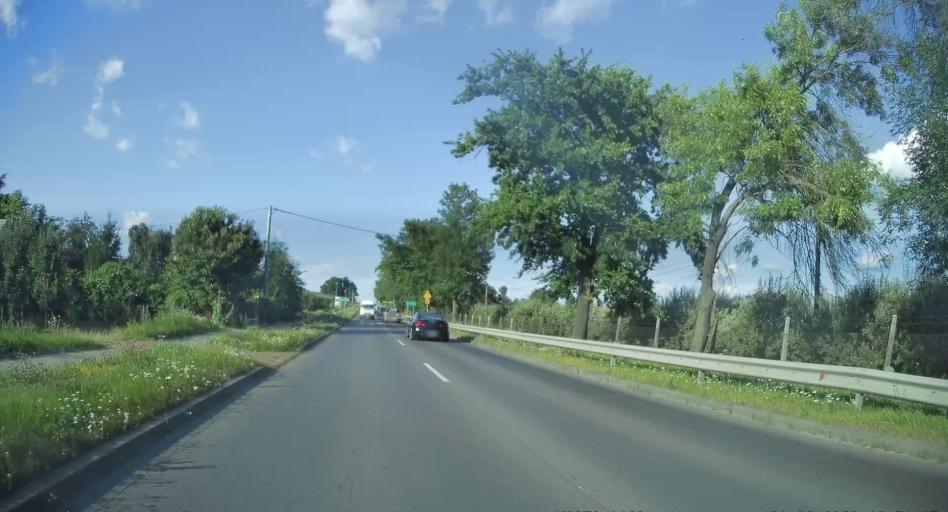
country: PL
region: Masovian Voivodeship
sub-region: Powiat grojecki
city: Belsk Duzy
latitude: 51.8330
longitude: 20.8187
